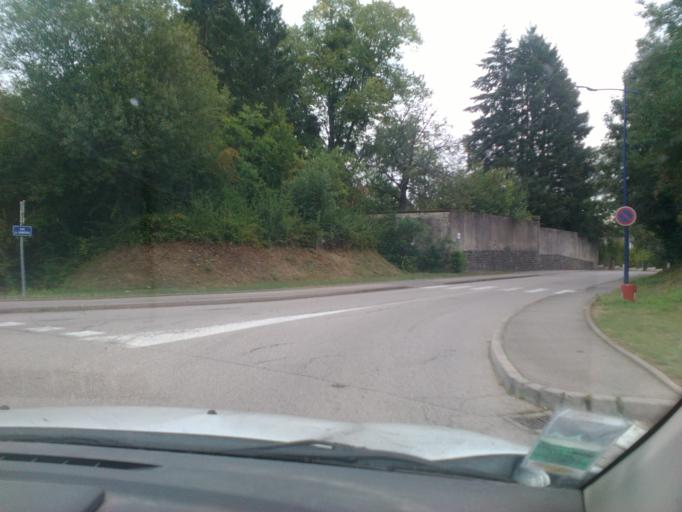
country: FR
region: Lorraine
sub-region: Departement des Vosges
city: Golbey
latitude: 48.1934
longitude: 6.4224
